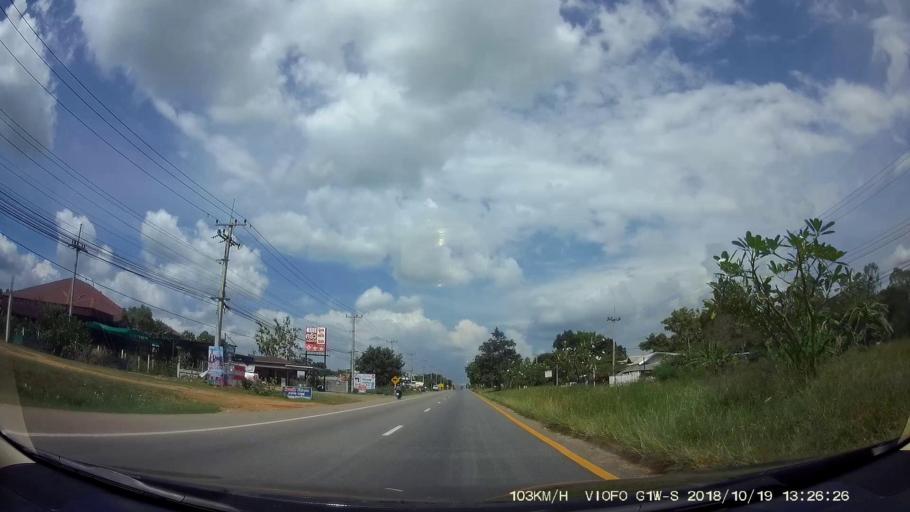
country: TH
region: Chaiyaphum
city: Chatturat
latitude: 15.5350
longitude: 101.8335
